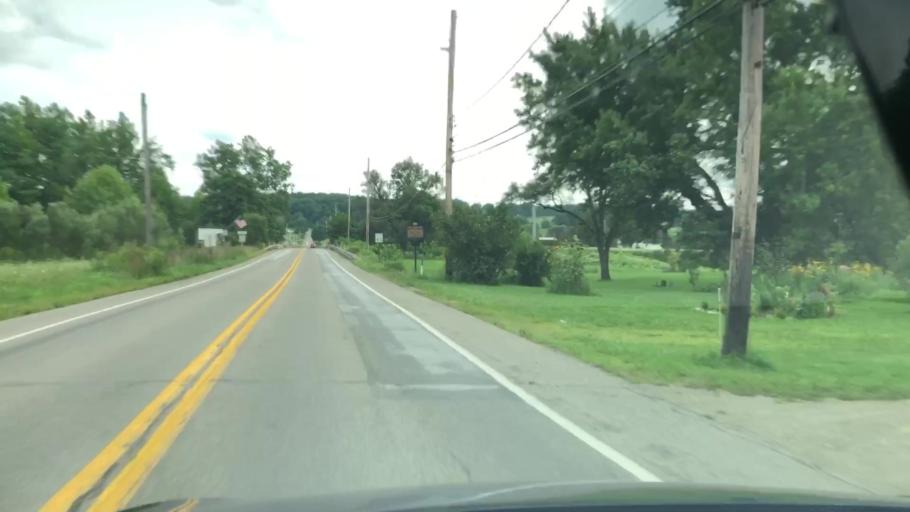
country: US
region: Pennsylvania
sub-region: Erie County
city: Union City
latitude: 41.9996
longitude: -79.8109
